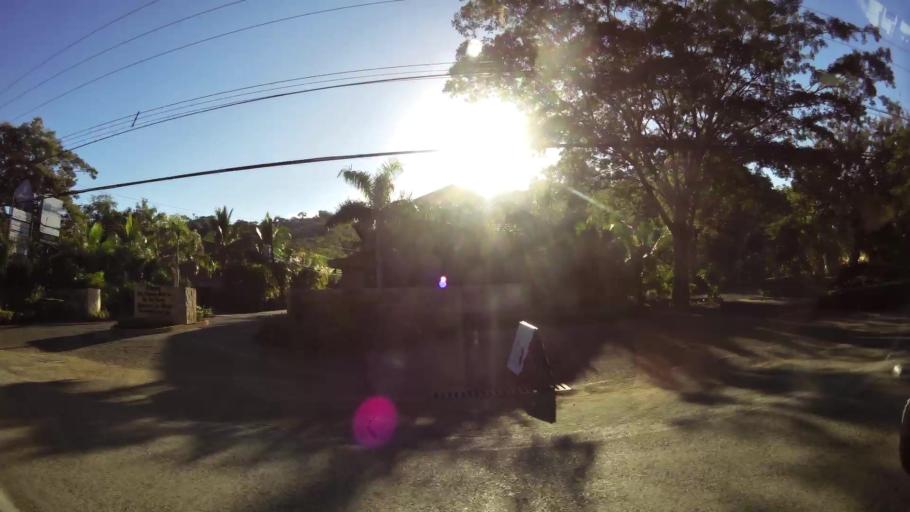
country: CR
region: Guanacaste
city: Sardinal
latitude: 10.5691
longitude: -85.6744
